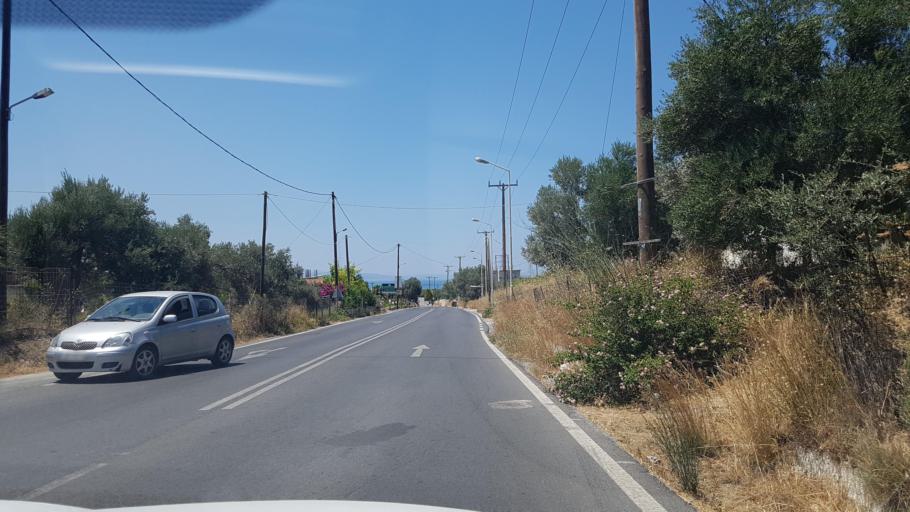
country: GR
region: Crete
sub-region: Nomos Rethymnis
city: Rethymno
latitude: 35.3579
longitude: 24.5543
